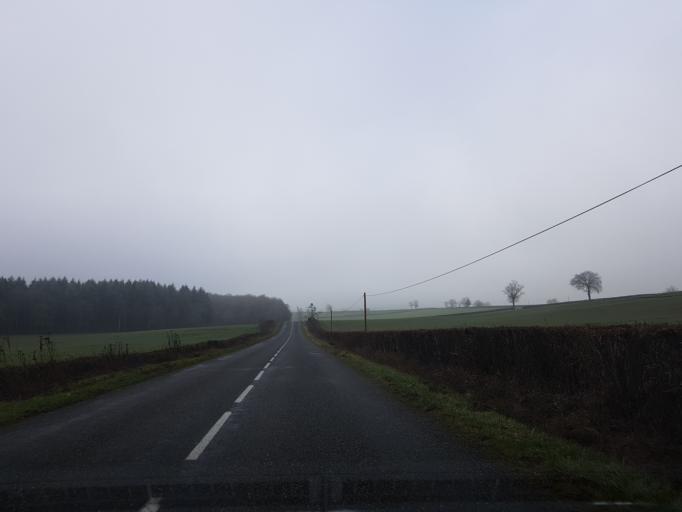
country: FR
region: Bourgogne
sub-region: Departement de Saone-et-Loire
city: Saint-Berain-sous-Sanvignes
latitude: 46.7298
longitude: 4.3227
